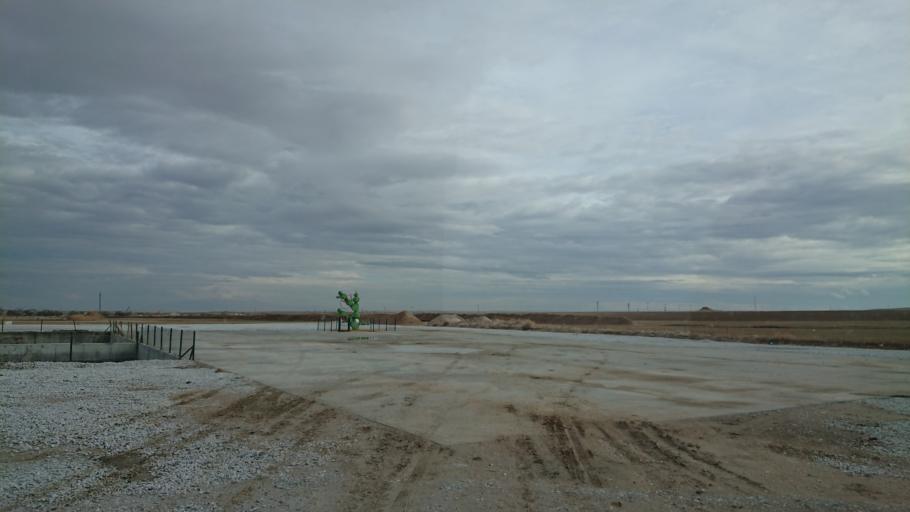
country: TR
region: Aksaray
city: Sultanhani
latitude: 38.1324
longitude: 33.5523
